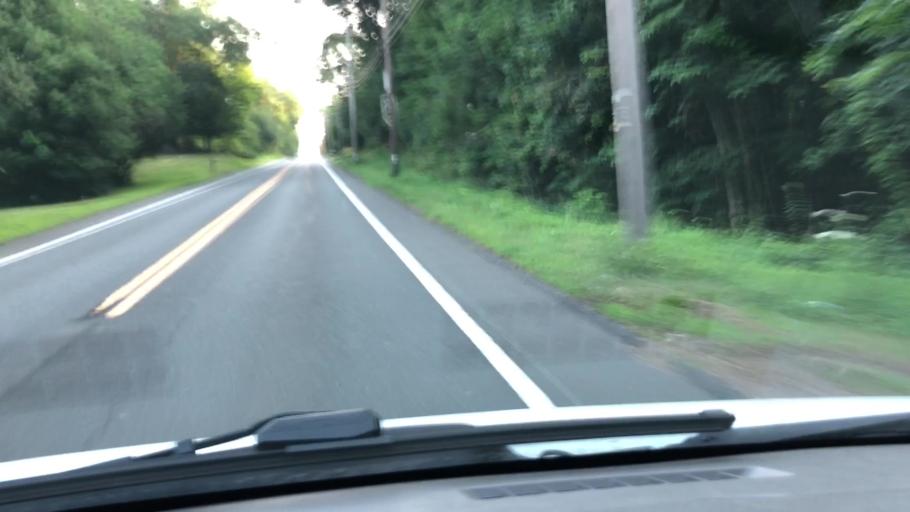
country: US
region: Massachusetts
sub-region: Hampshire County
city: Williamsburg
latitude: 42.3559
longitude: -72.6917
